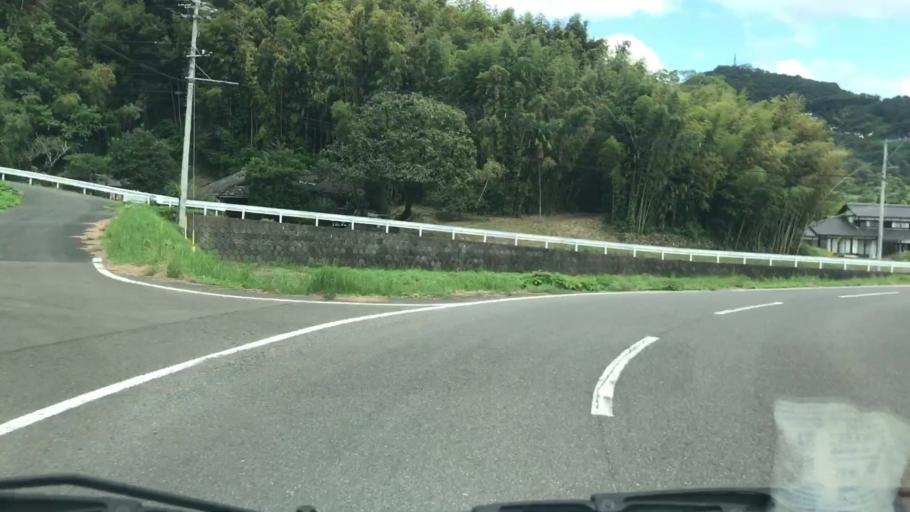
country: JP
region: Saga Prefecture
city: Takeocho-takeo
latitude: 33.2311
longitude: 130.1486
